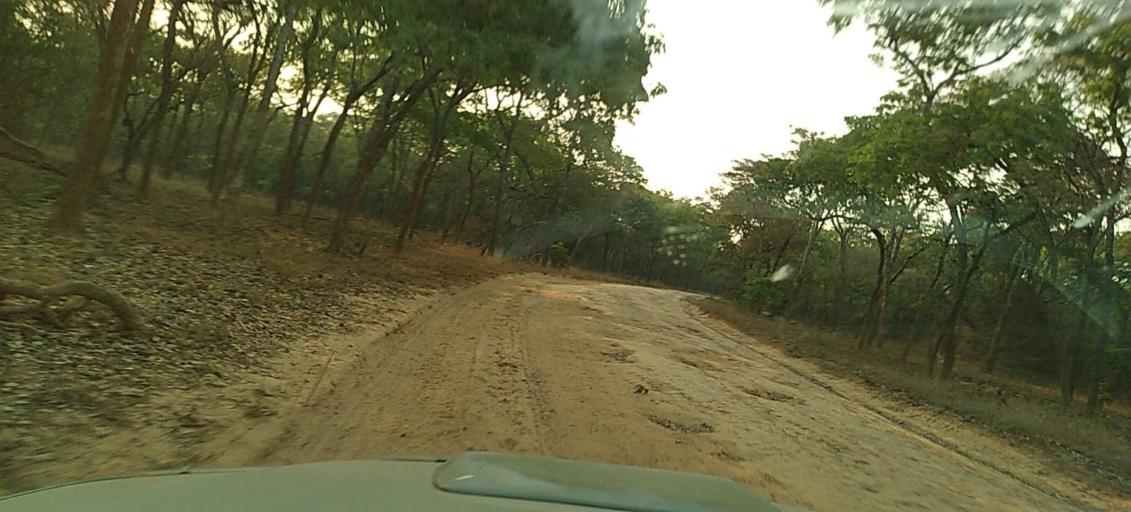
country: ZM
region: North-Western
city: Kasempa
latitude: -13.1552
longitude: 26.4435
